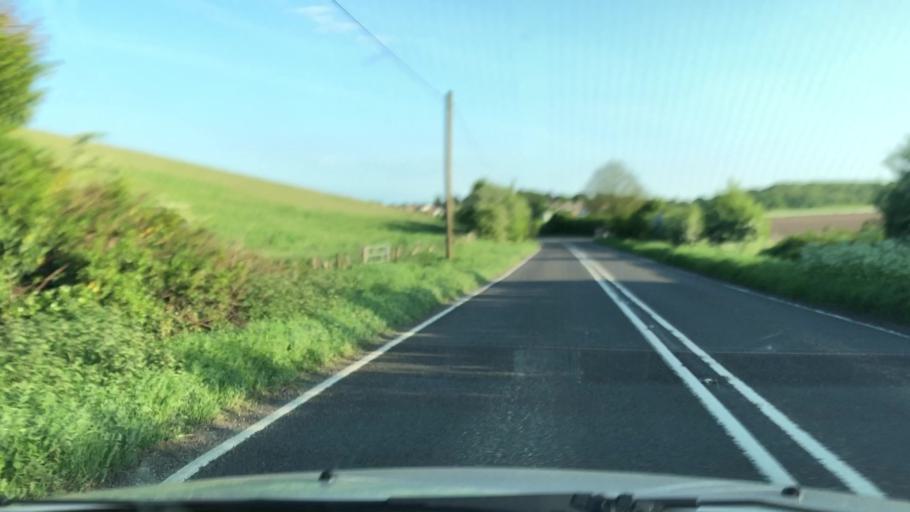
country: GB
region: England
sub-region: Hampshire
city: Alton
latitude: 51.1549
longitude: -0.9891
